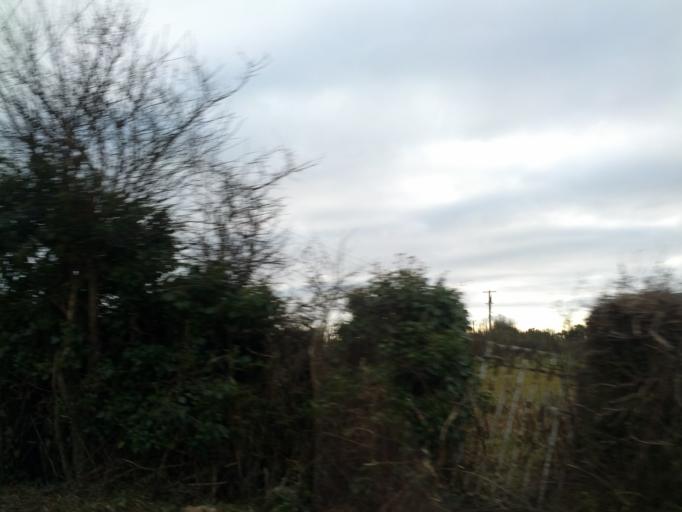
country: IE
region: Connaught
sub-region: County Galway
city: Oranmore
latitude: 53.1803
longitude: -8.9041
